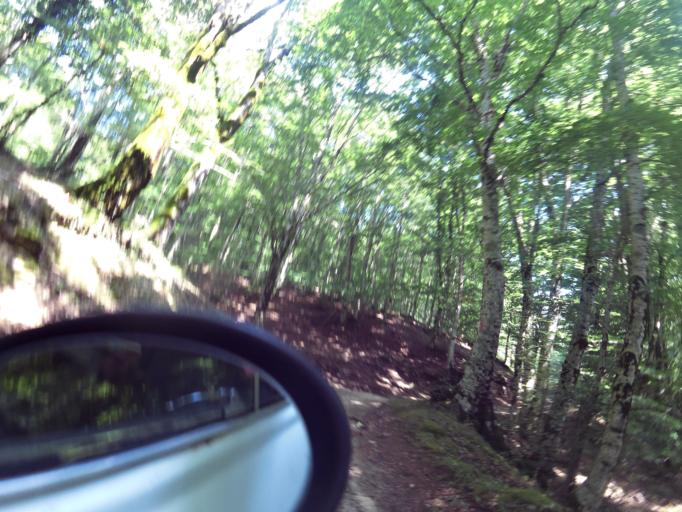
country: IT
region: Calabria
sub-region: Provincia di Vibo-Valentia
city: Nardodipace
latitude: 38.5099
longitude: 16.3816
